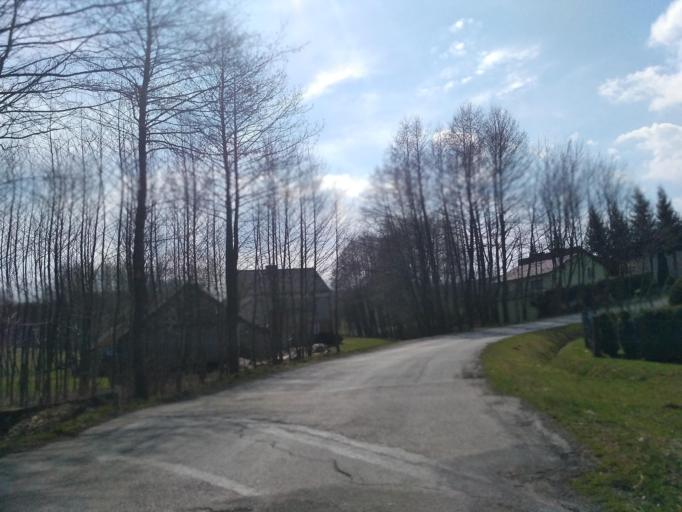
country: PL
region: Subcarpathian Voivodeship
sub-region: Powiat ropczycko-sedziszowski
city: Iwierzyce
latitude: 49.9983
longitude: 21.7555
